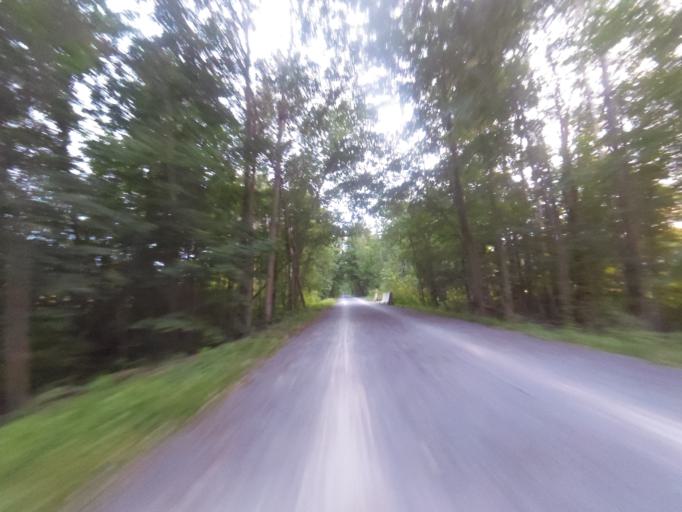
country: CA
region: Ontario
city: Bells Corners
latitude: 45.2723
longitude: -75.8984
